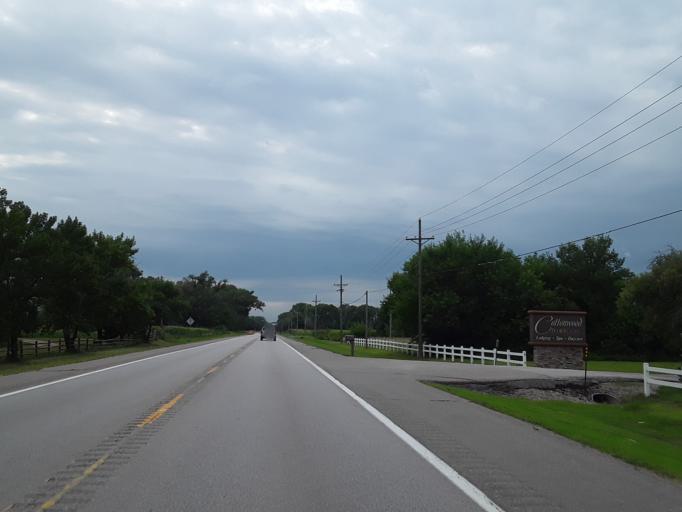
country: US
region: Nebraska
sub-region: Saunders County
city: Yutan
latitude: 41.2338
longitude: -96.3383
